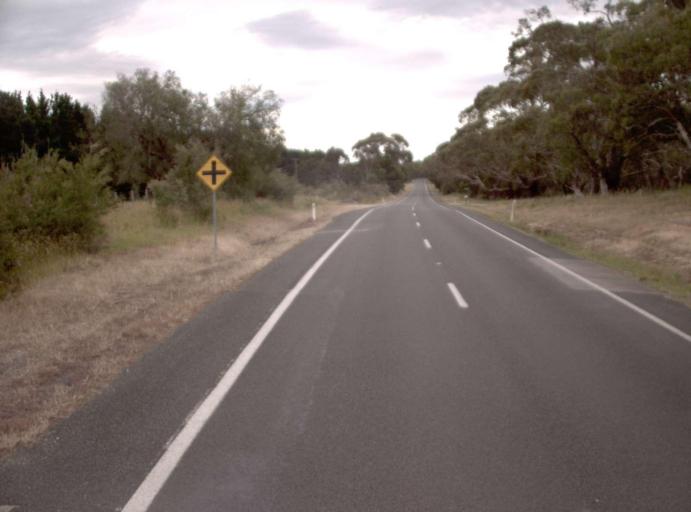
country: AU
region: Victoria
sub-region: Wellington
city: Sale
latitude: -38.2207
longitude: 147.0584
